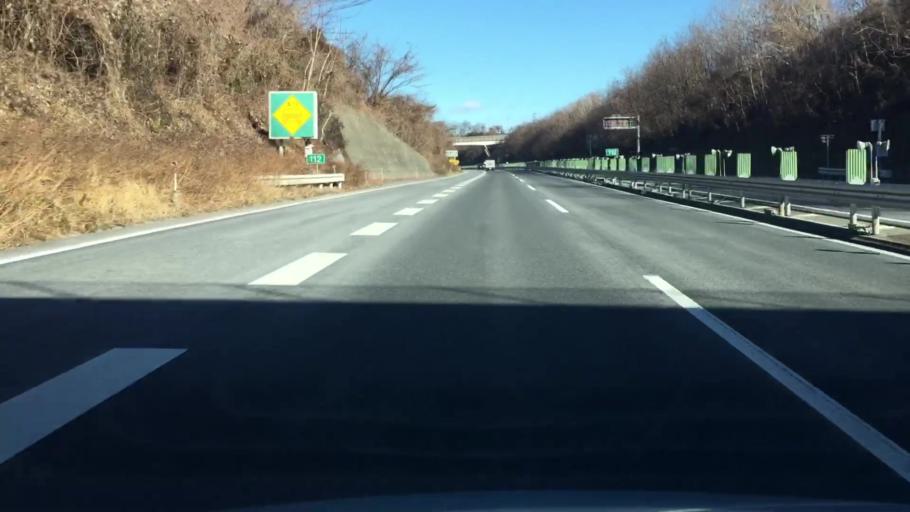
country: JP
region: Gunma
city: Shibukawa
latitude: 36.5419
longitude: 139.0504
